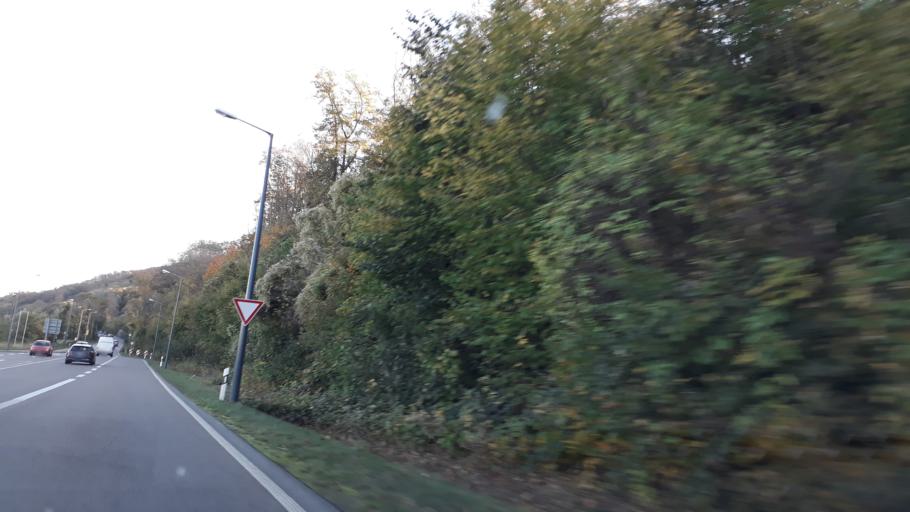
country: DE
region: Saxony
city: Coswig
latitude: 51.0918
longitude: 13.6065
